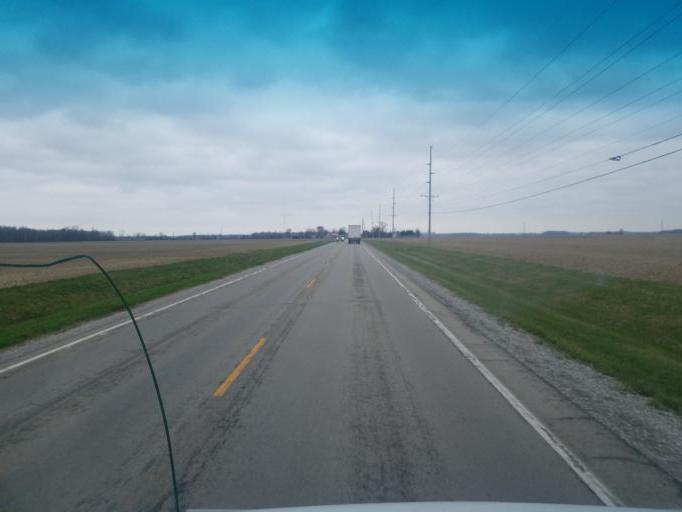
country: US
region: Ohio
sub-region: Defiance County
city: Hicksville
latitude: 41.2495
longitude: -84.7578
